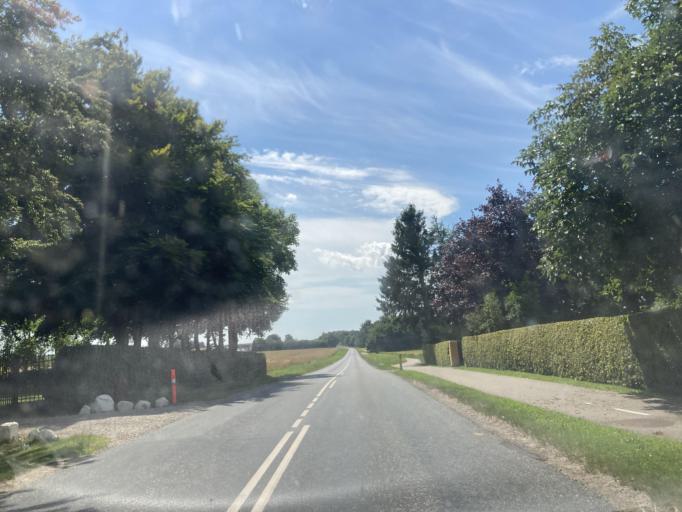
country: DK
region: Zealand
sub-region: Faxe Kommune
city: Haslev
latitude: 55.3707
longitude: 11.9619
